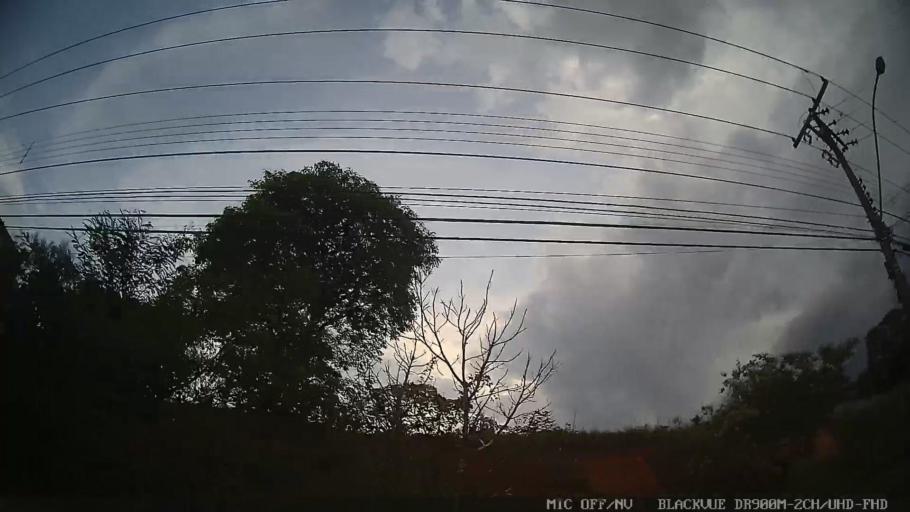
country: BR
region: Sao Paulo
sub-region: Itatiba
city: Itatiba
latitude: -22.9919
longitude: -46.8457
